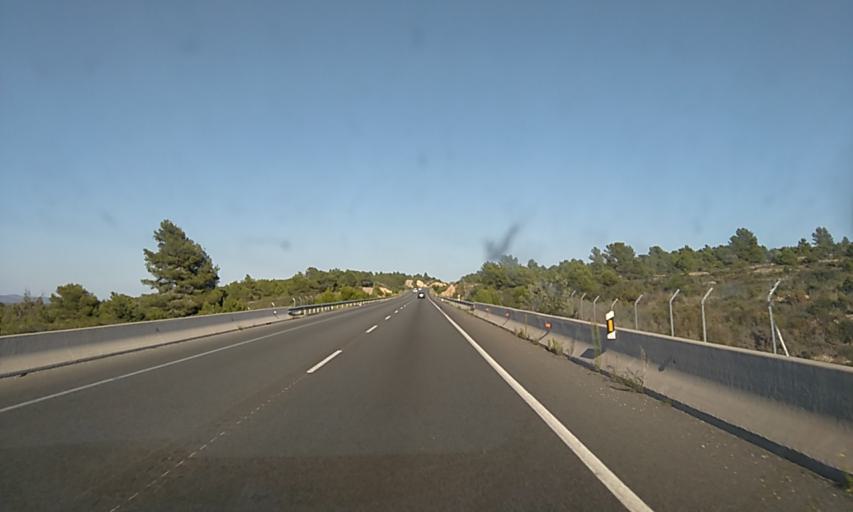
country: ES
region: Valencia
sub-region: Provincia de Castello
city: Torreblanca
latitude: 40.2173
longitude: 0.1574
